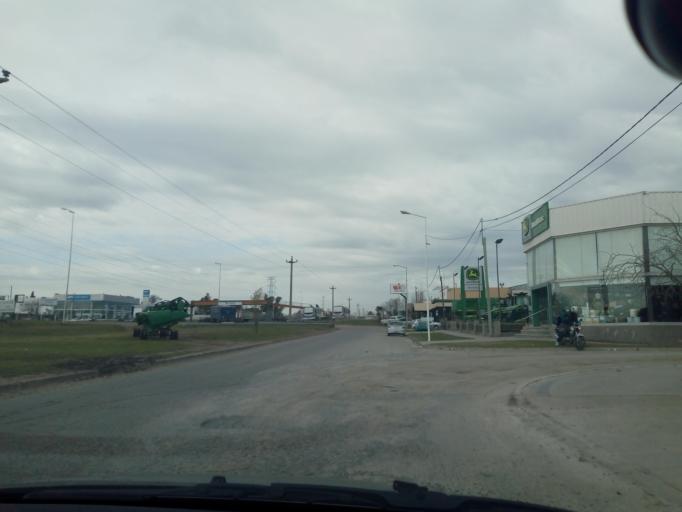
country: AR
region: Buenos Aires
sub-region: Partido de Tandil
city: Tandil
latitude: -37.3137
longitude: -59.1121
